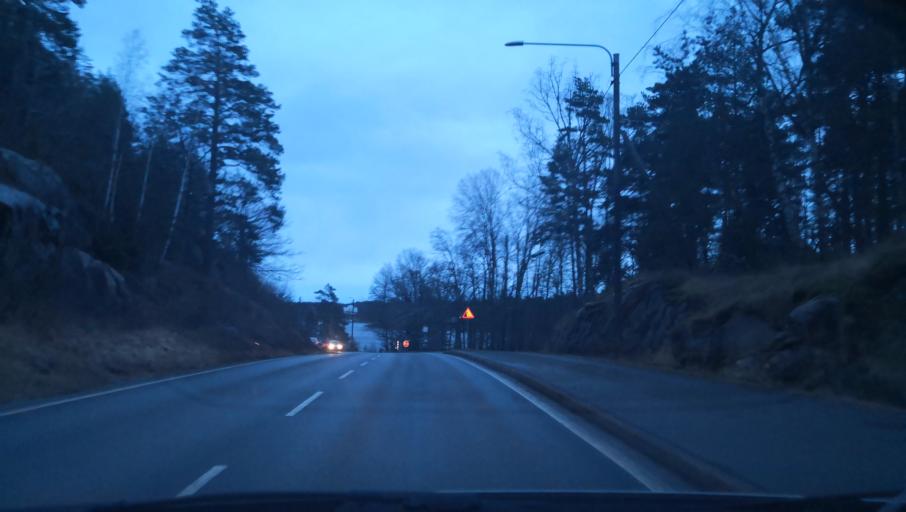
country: SE
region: Stockholm
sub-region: Varmdo Kommun
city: Gustavsberg
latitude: 59.3282
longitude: 18.3546
